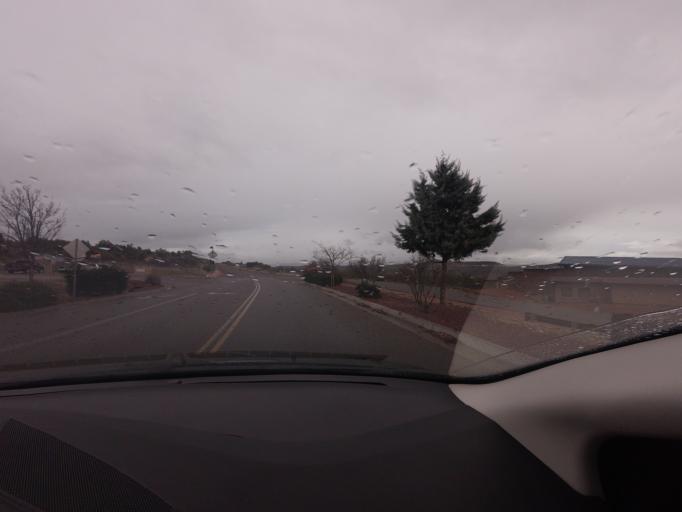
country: US
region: Arizona
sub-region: Yavapai County
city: Camp Verde
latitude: 34.6050
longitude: -111.8581
